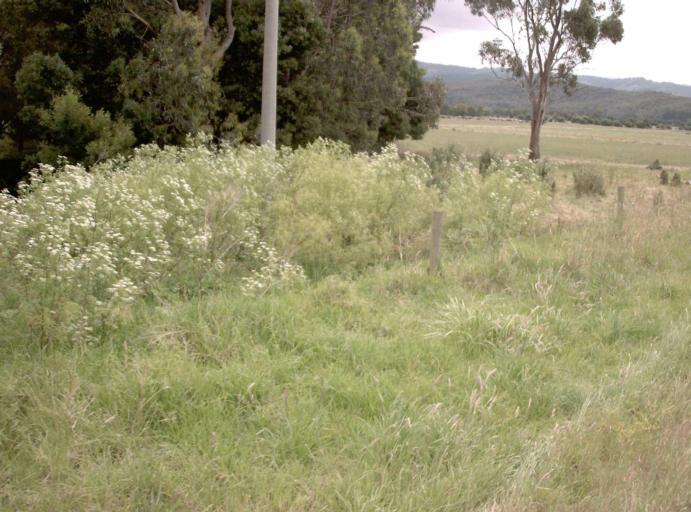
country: AU
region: Victoria
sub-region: Latrobe
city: Traralgon
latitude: -38.5105
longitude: 146.6630
